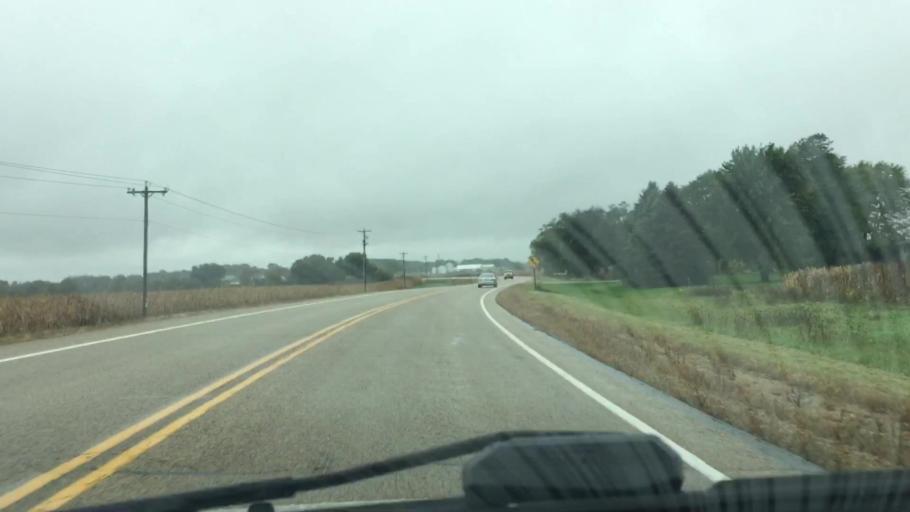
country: US
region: Wisconsin
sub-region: Jefferson County
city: Palmyra
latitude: 42.8605
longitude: -88.6541
